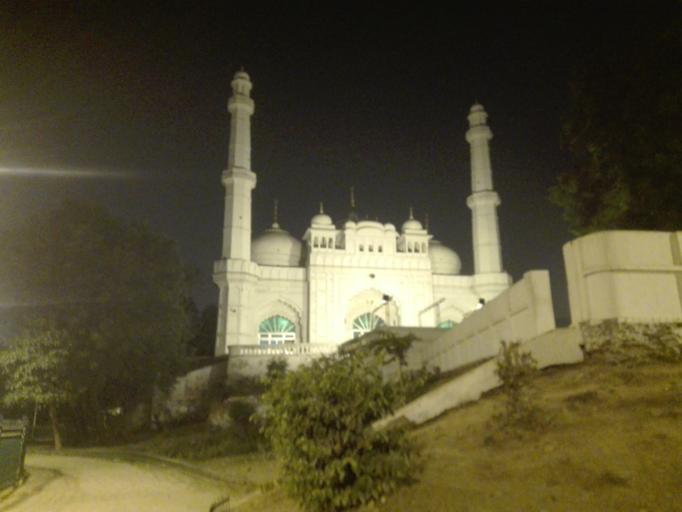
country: IN
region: Uttar Pradesh
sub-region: Lucknow District
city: Lucknow
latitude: 26.8715
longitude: 80.9149
